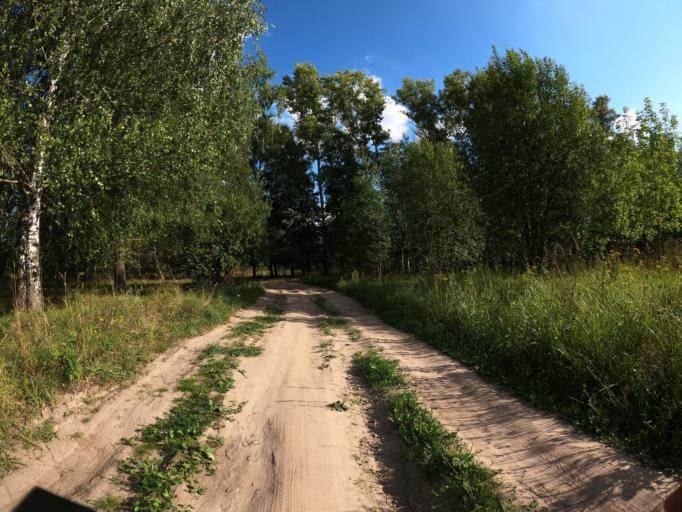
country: RU
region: Moskovskaya
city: Peski
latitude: 55.1927
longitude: 38.7470
